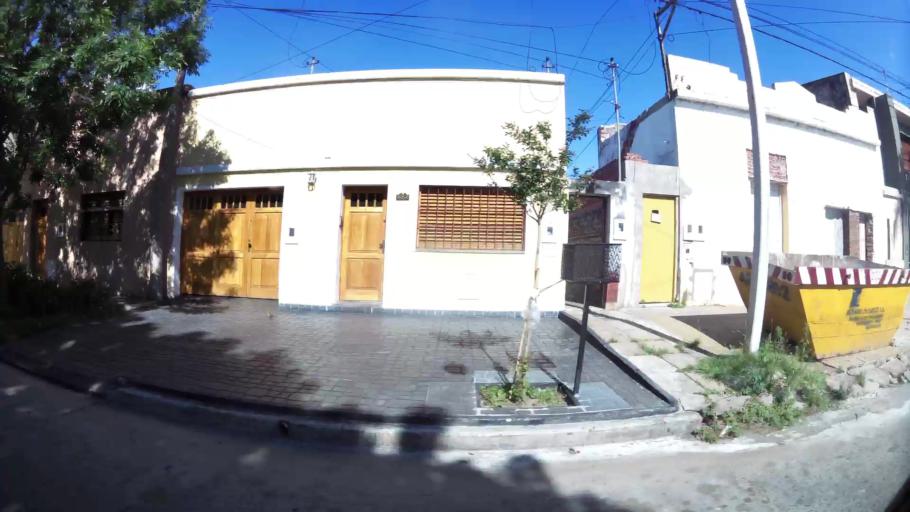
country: AR
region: Santa Fe
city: Santa Fe de la Vera Cruz
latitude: -31.6332
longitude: -60.6897
